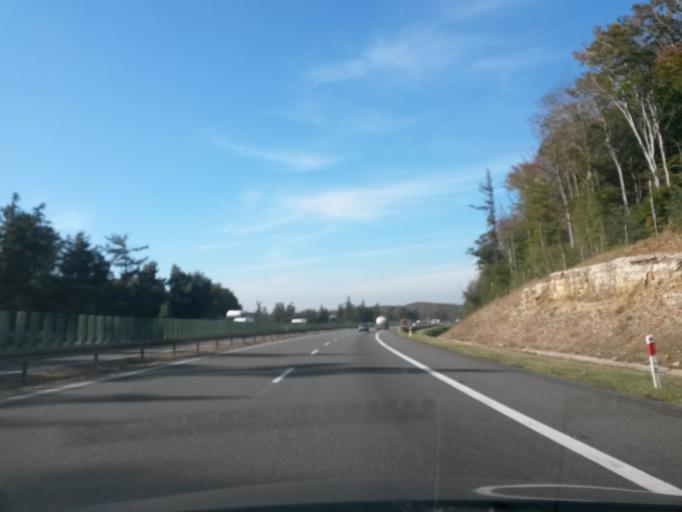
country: PL
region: Opole Voivodeship
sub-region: Powiat krapkowicki
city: Zdzieszowice
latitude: 50.4717
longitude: 18.1413
